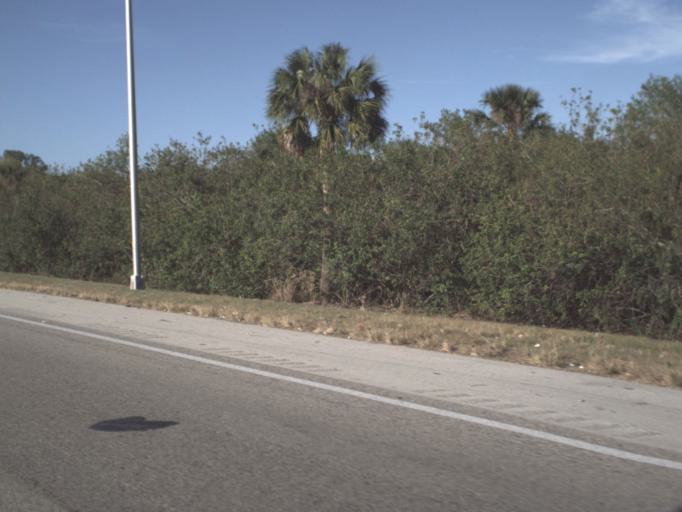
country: US
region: Florida
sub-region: Brevard County
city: June Park
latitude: 28.0872
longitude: -80.7058
